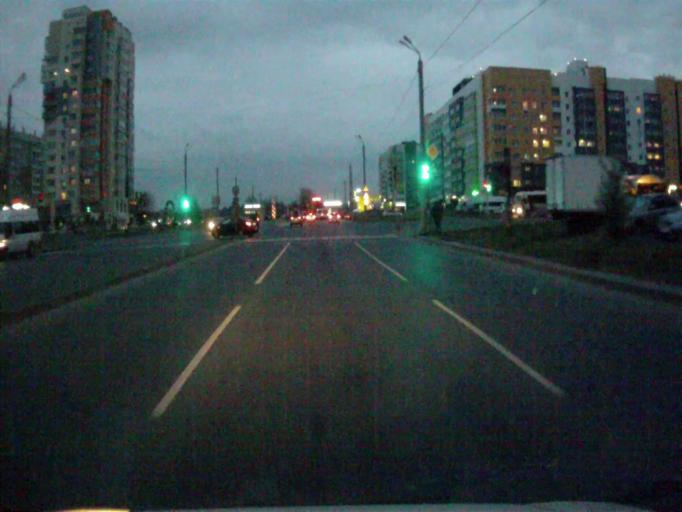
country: RU
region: Chelyabinsk
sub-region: Gorod Chelyabinsk
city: Chelyabinsk
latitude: 55.1638
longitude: 61.2949
